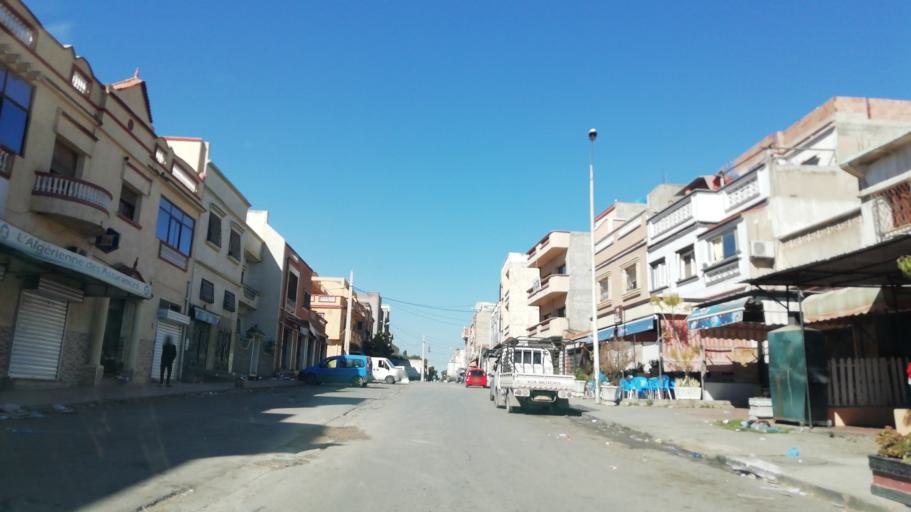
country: DZ
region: Oran
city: Oran
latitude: 35.6903
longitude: -0.6151
